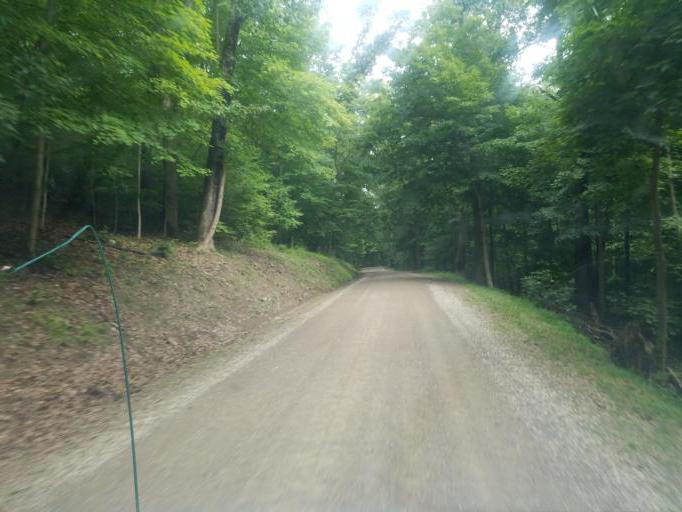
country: US
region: Ohio
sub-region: Knox County
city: Oak Hill
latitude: 40.4036
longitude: -82.1842
